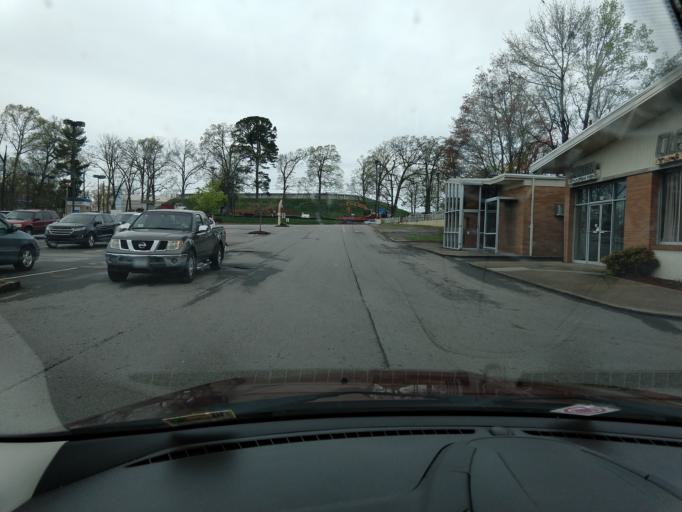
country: US
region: Virginia
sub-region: City of Danville
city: Danville
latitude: 36.5717
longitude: -79.4182
